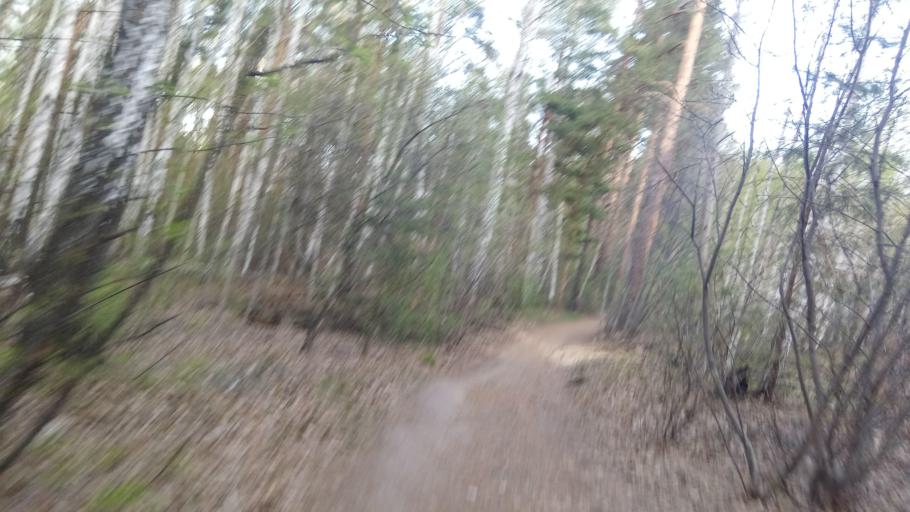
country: RU
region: Chelyabinsk
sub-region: Gorod Chelyabinsk
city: Chelyabinsk
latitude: 55.1648
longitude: 61.3224
